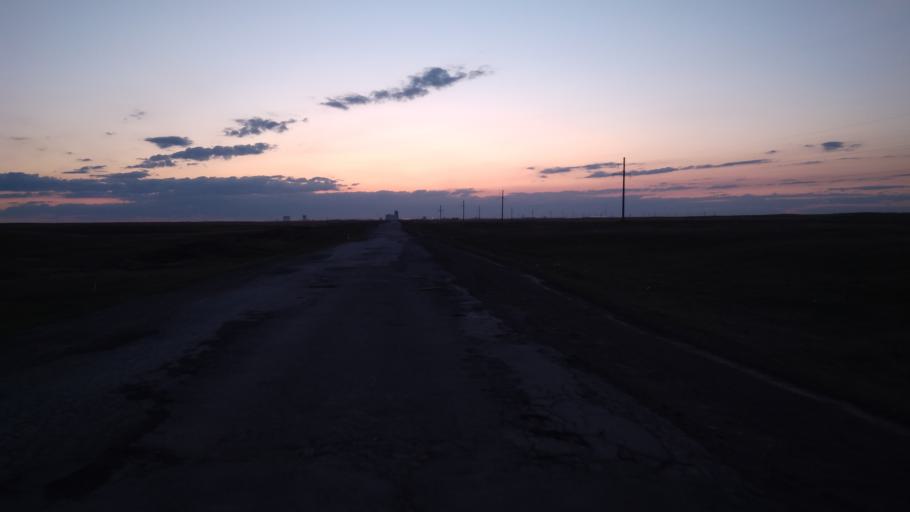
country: RU
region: Chelyabinsk
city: Troitsk
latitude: 54.0900
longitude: 61.6480
